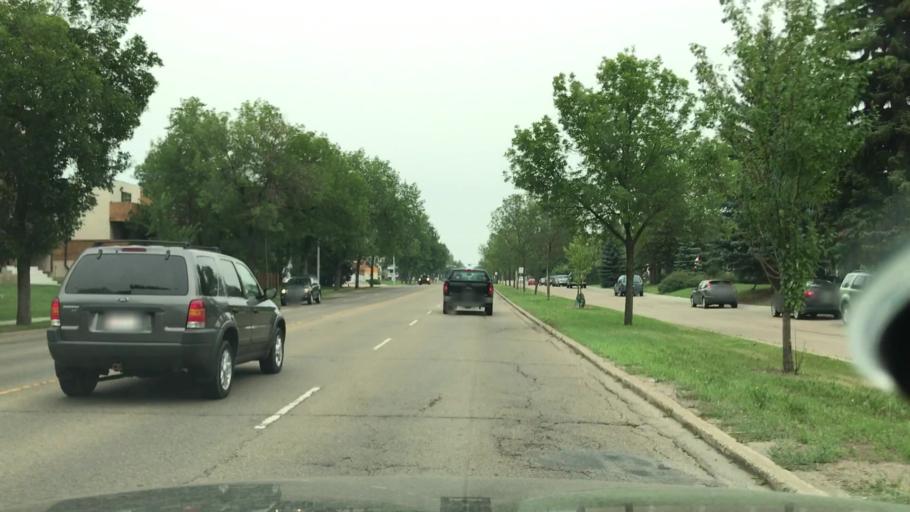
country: CA
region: Alberta
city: Edmonton
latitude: 53.5255
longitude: -113.5779
